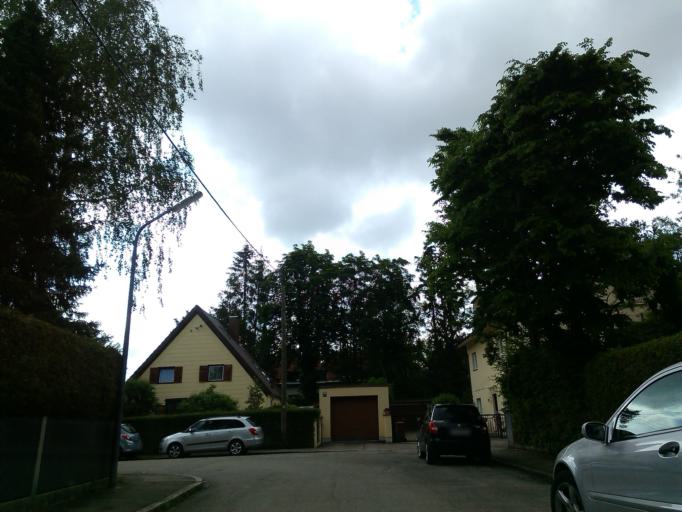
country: DE
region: Bavaria
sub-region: Upper Bavaria
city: Neuried
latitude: 48.0860
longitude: 11.4752
